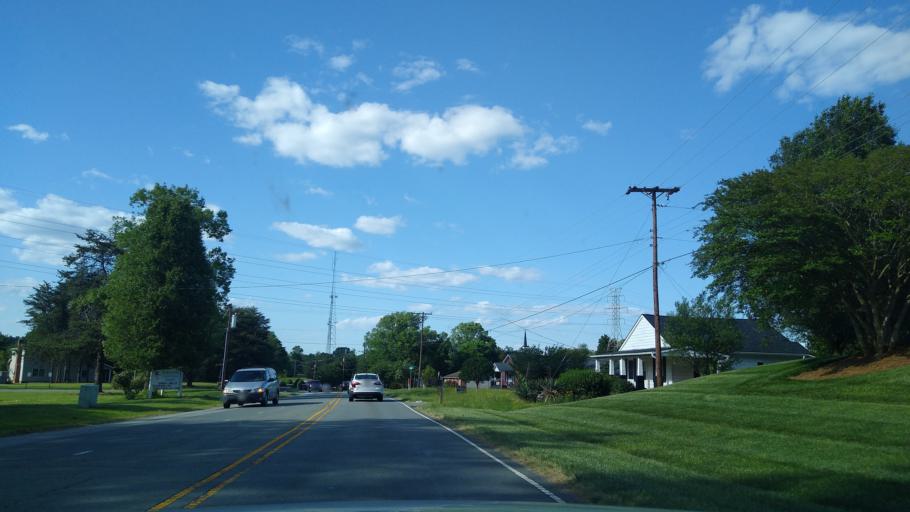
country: US
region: North Carolina
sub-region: Forsyth County
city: Kernersville
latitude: 36.1031
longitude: -80.0783
